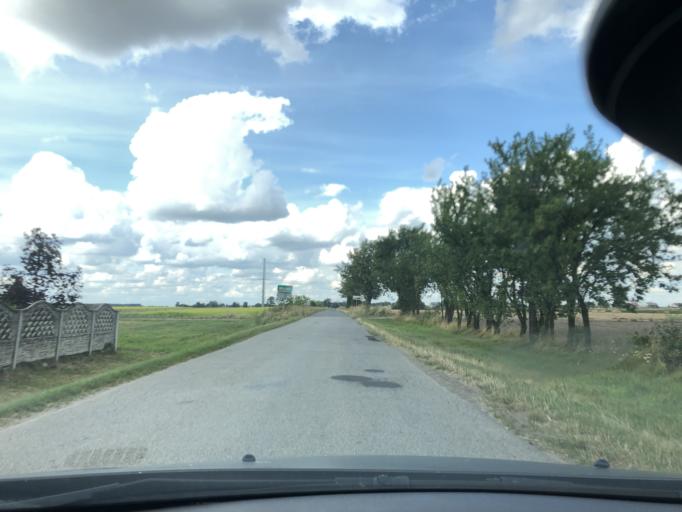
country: PL
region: Lodz Voivodeship
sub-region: Powiat wieruszowski
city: Walichnowy
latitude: 51.2382
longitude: 18.3880
